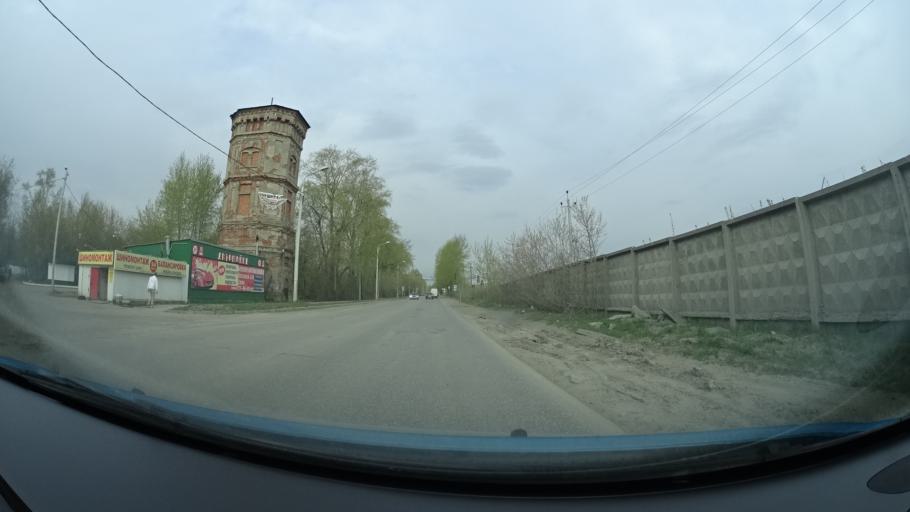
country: RU
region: Perm
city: Kondratovo
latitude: 58.0023
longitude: 56.1734
